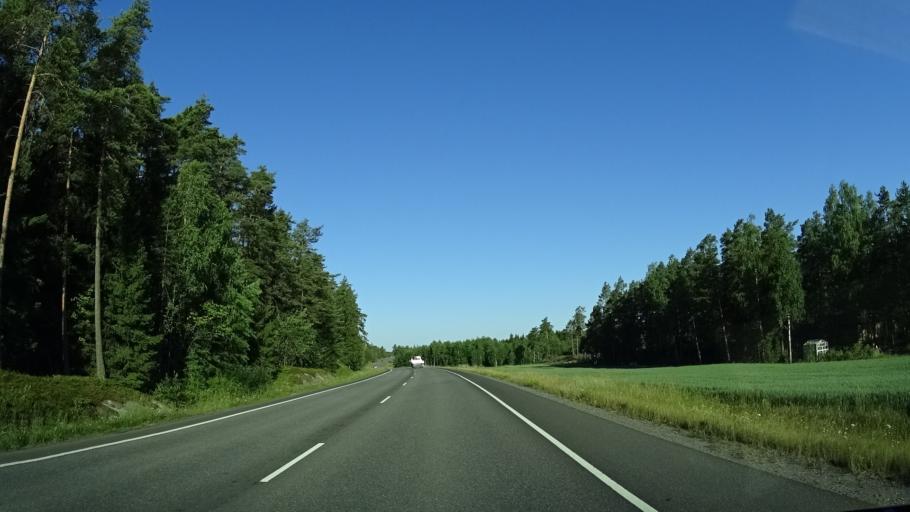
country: FI
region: Varsinais-Suomi
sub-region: Turku
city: Merimasku
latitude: 60.4605
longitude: 21.9434
